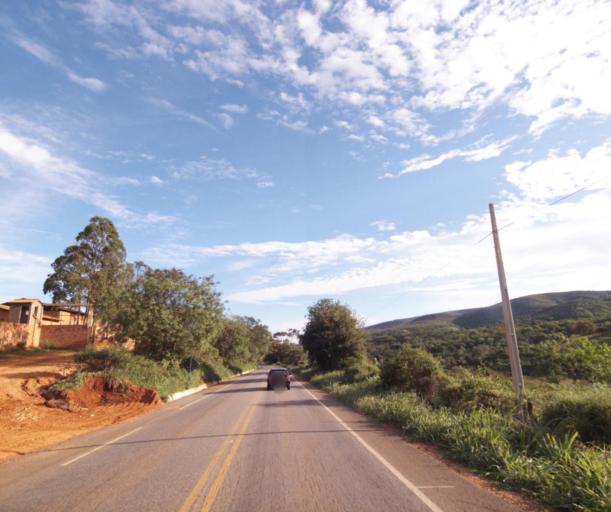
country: BR
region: Bahia
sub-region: Caetite
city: Caetite
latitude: -14.0752
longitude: -42.4572
